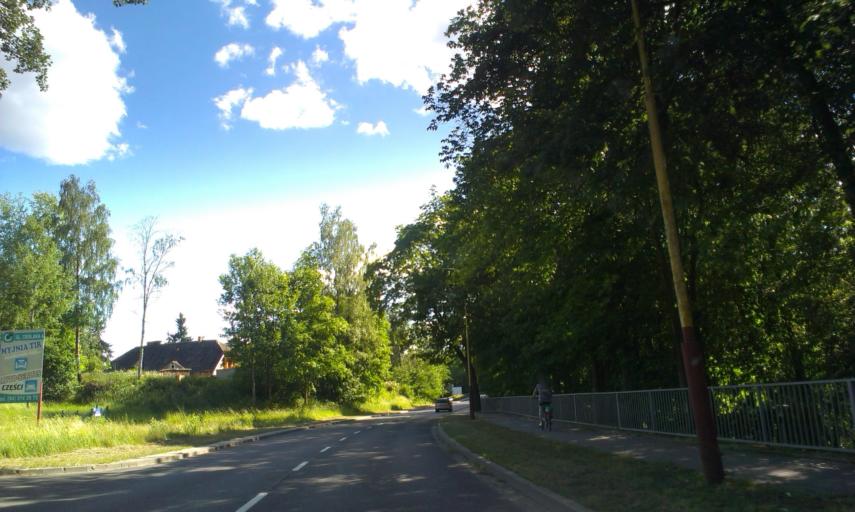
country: PL
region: West Pomeranian Voivodeship
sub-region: Powiat szczecinecki
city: Szczecinek
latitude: 53.6871
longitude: 16.6915
